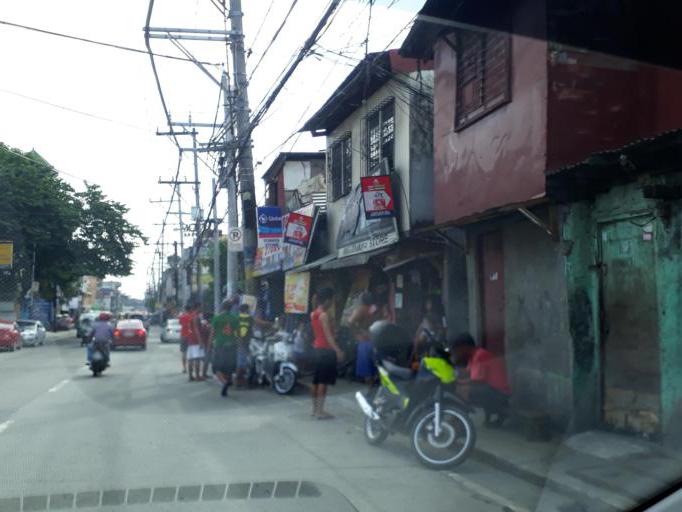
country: PH
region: Metro Manila
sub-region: Caloocan City
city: Niugan
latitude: 14.6701
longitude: 120.9714
